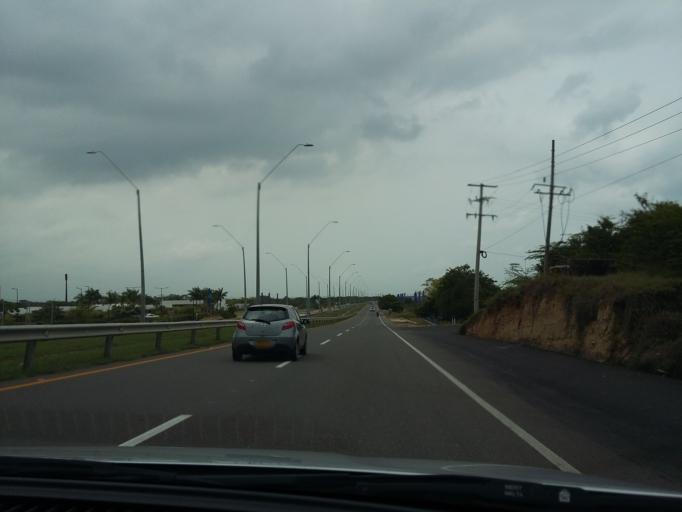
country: CO
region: Bolivar
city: Cartagena
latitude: 10.5082
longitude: -75.4721
